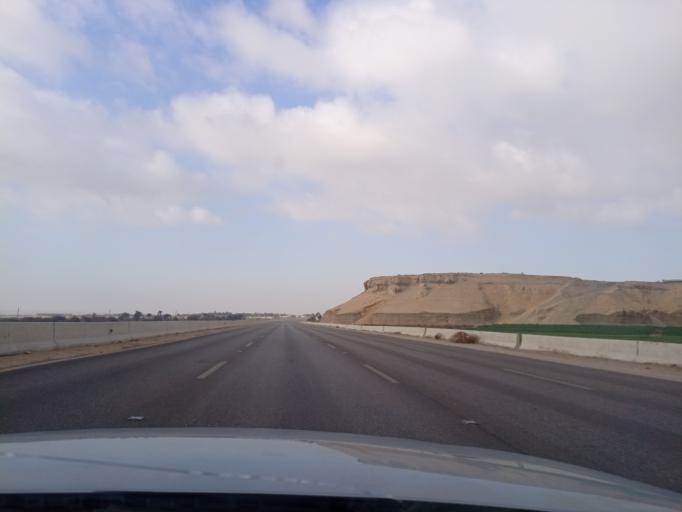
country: EG
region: Al Jizah
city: Al `Ayyat
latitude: 29.6772
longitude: 31.2081
